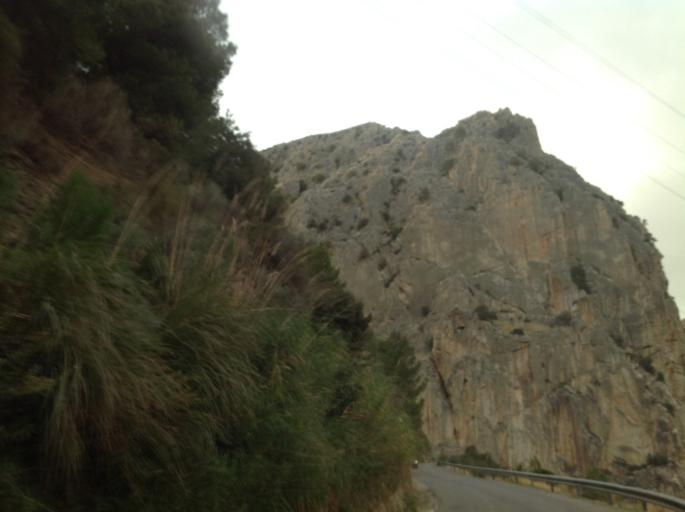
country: ES
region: Andalusia
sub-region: Provincia de Malaga
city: Carratraca
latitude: 36.9133
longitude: -4.7716
